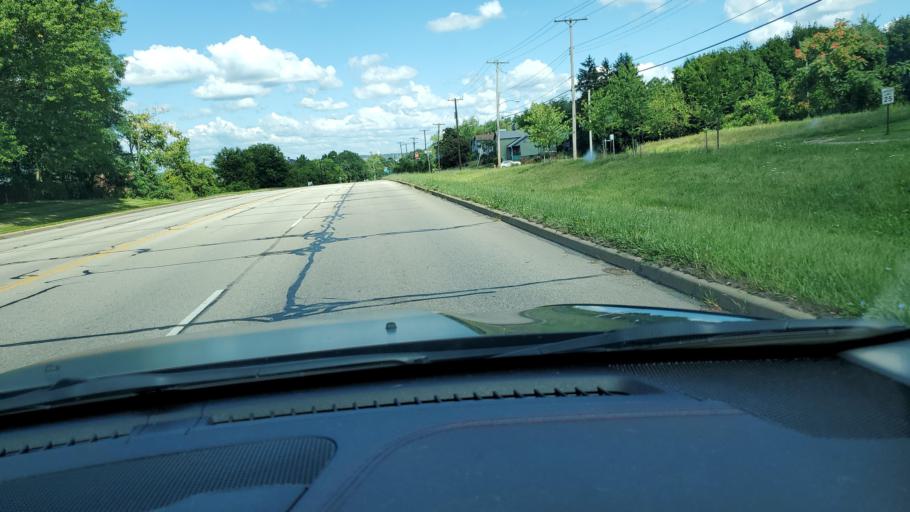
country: US
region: Ohio
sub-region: Mahoning County
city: Youngstown
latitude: 41.1172
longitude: -80.6711
